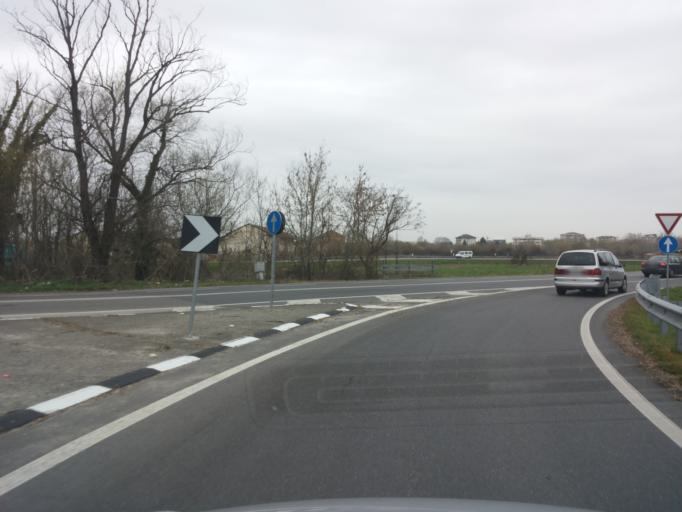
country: IT
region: Piedmont
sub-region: Provincia di Vercelli
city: Vercelli
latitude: 45.3096
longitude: 8.4030
